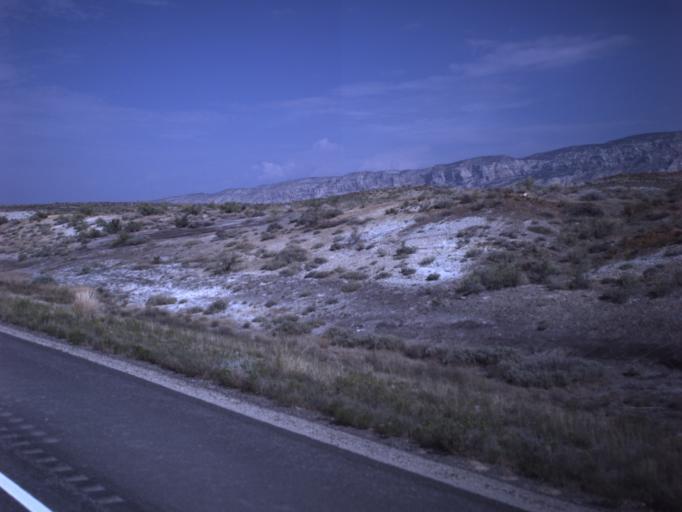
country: US
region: Colorado
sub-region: Rio Blanco County
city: Rangely
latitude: 40.2860
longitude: -109.1300
